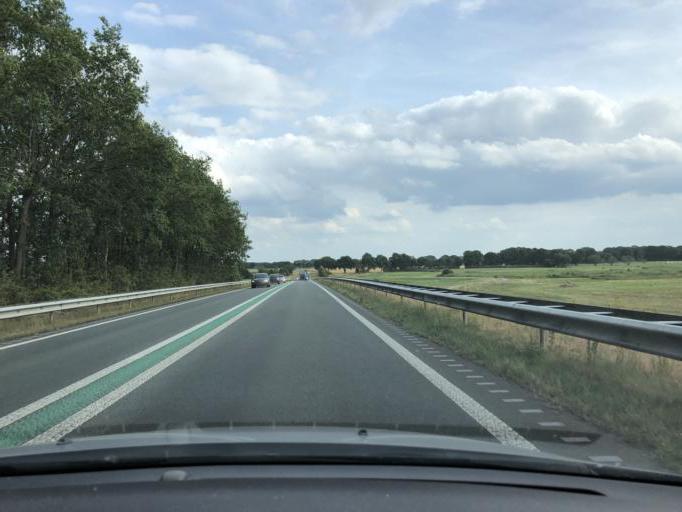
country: NL
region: Drenthe
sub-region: Gemeente Borger-Odoorn
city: Borger
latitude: 52.9144
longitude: 6.7922
